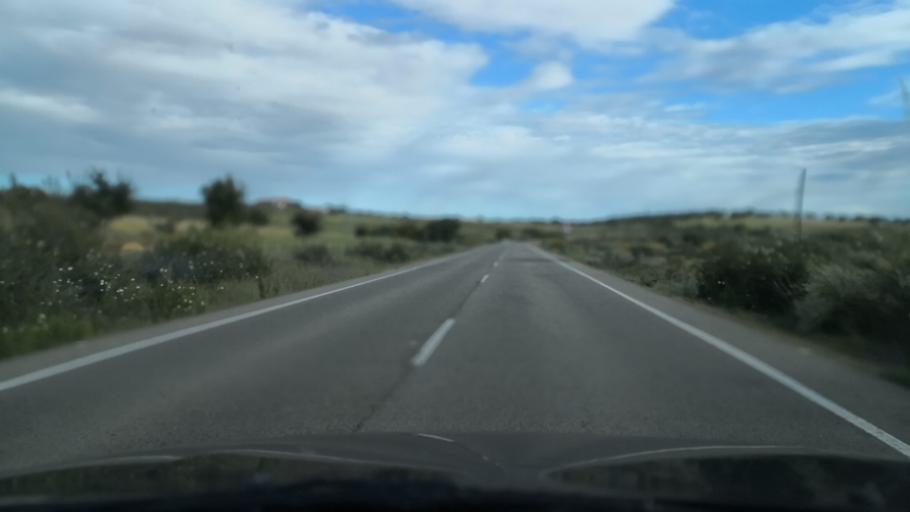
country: ES
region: Extremadura
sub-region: Provincia de Caceres
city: Perales del Puerto
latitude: 40.1184
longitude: -6.6714
